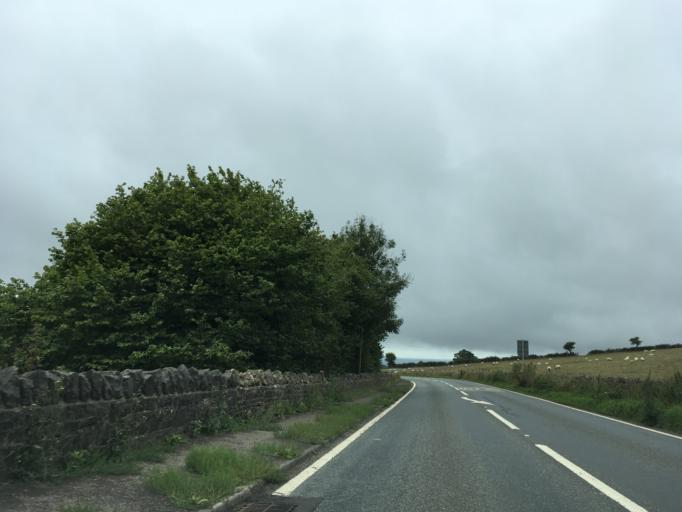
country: GB
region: England
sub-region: Somerset
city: Mendip
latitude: 51.2261
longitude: -2.6225
